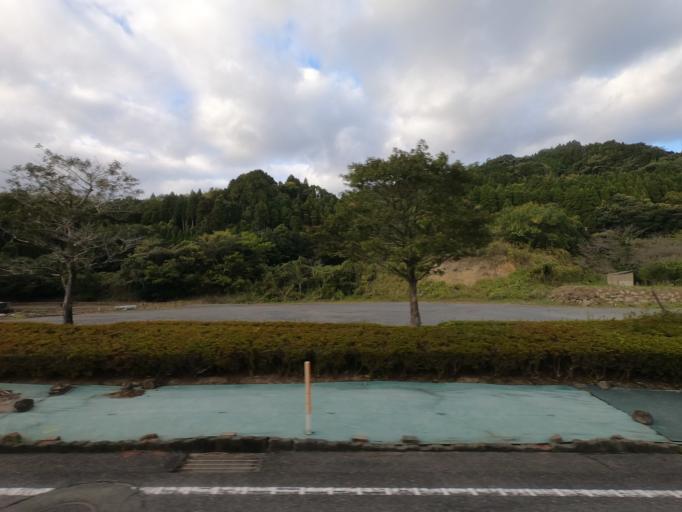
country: JP
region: Kumamoto
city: Minamata
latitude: 32.2456
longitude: 130.4733
